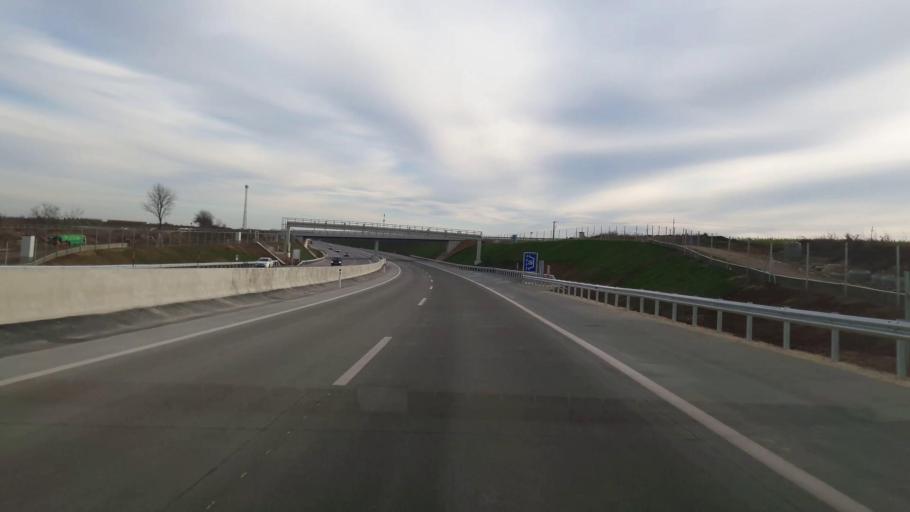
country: AT
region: Lower Austria
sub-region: Politischer Bezirk Mistelbach
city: Herrnbaumgarten
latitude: 48.6821
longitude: 16.6588
